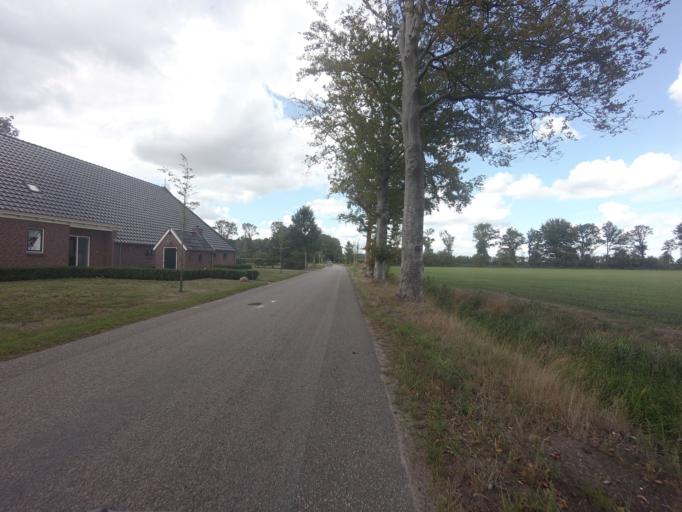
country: NL
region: Drenthe
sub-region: Gemeente Westerveld
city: Dwingeloo
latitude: 52.9569
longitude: 6.3032
